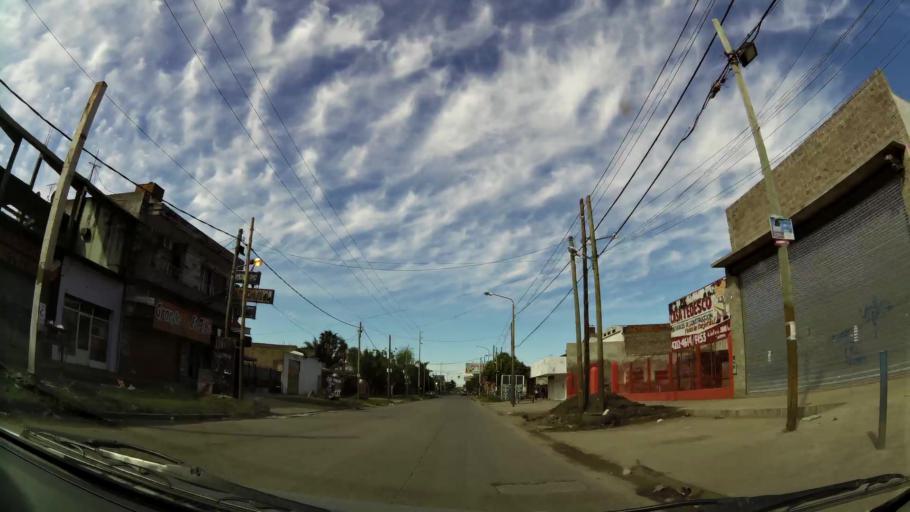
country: AR
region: Buenos Aires
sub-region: Partido de Quilmes
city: Quilmes
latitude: -34.7678
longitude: -58.3144
